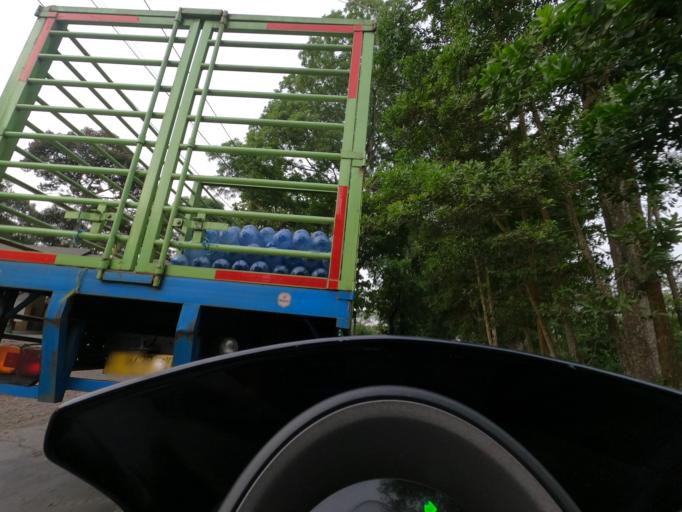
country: ID
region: West Java
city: Lembang
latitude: -6.6728
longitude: 107.6970
